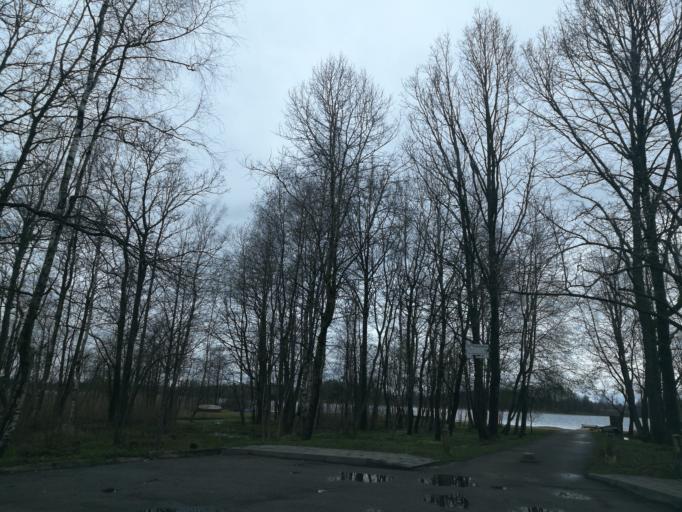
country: LT
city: Rietavas
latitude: 55.7018
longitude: 21.7340
